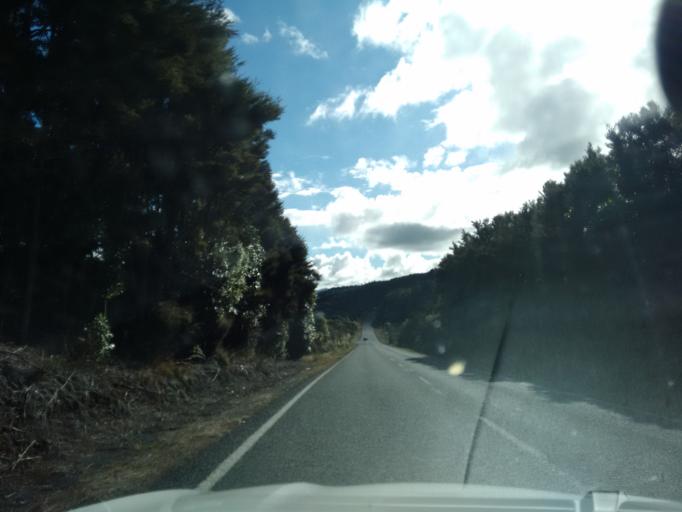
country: NZ
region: Waikato
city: Turangi
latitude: -39.0235
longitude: 175.7228
